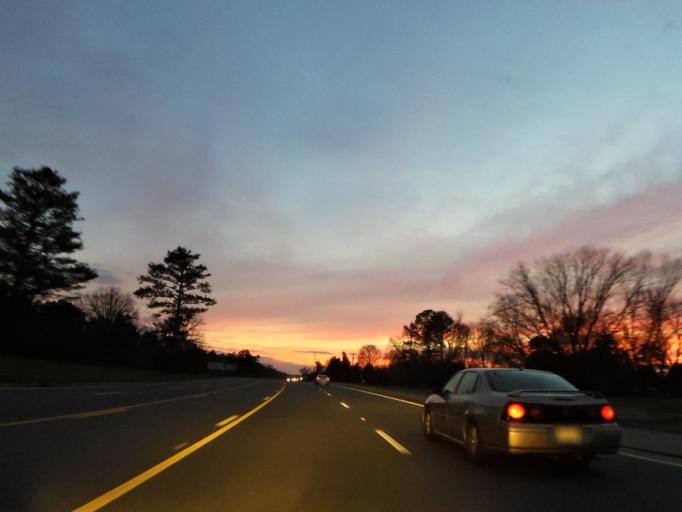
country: US
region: Tennessee
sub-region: Polk County
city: Benton
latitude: 35.1430
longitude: -84.7088
